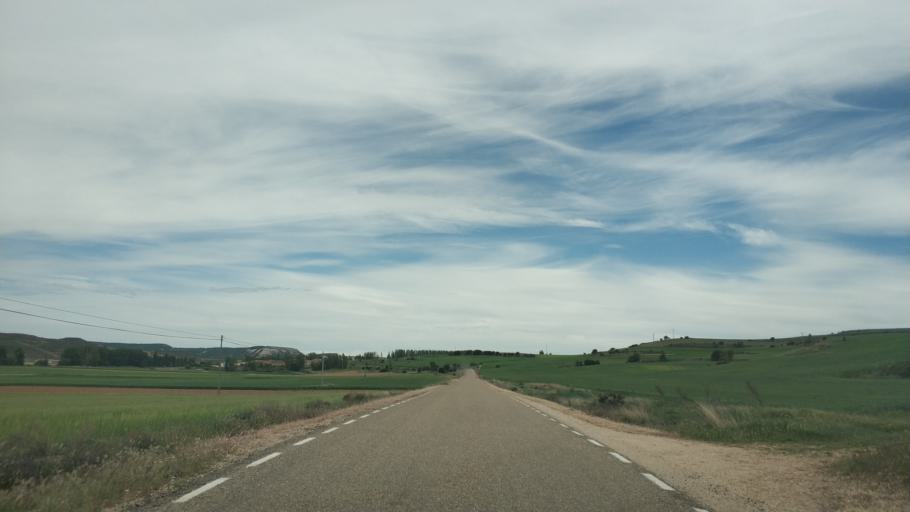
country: ES
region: Castille and Leon
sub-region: Provincia de Soria
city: Berlanga de Duero
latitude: 41.4462
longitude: -2.8333
